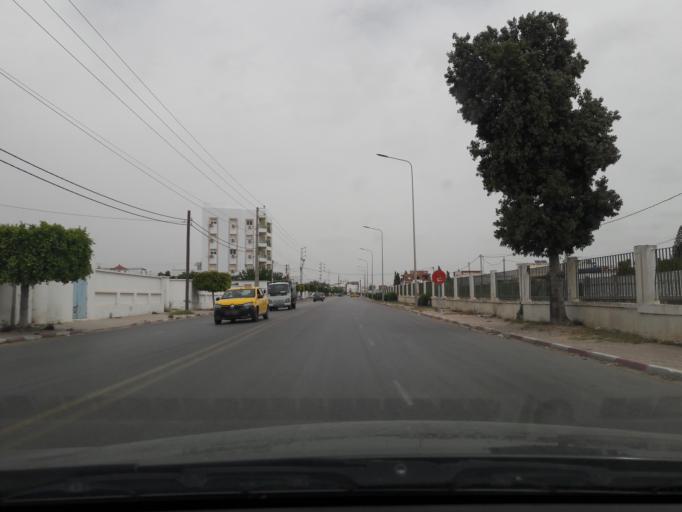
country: TN
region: Safaqis
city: Al Qarmadah
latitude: 34.7899
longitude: 10.7601
